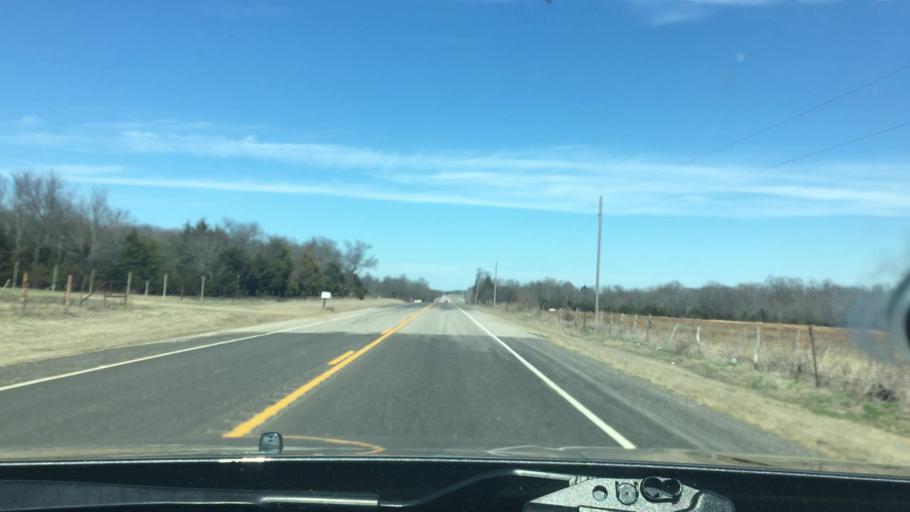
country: US
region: Oklahoma
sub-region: Murray County
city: Sulphur
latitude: 34.3558
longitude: -96.9509
